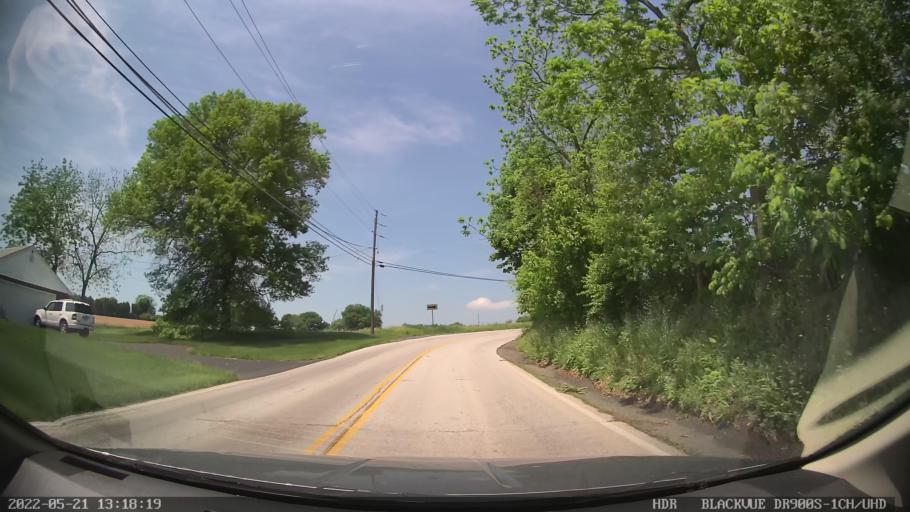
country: US
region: Pennsylvania
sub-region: Berks County
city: Bally
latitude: 40.3670
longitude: -75.5940
